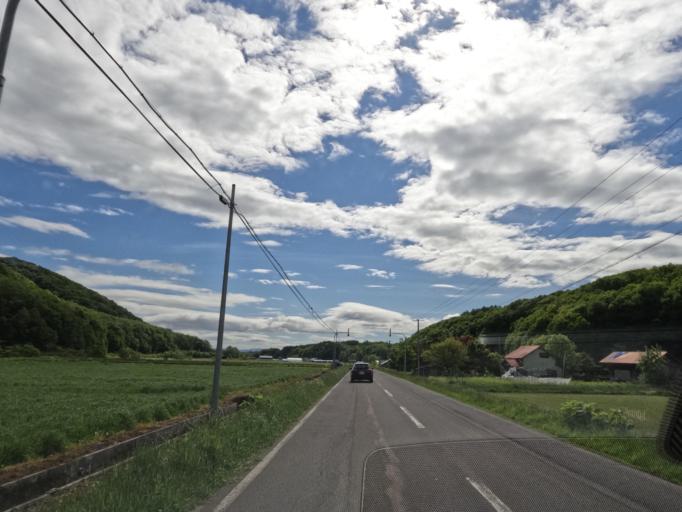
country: JP
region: Hokkaido
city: Kamikawa
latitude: 43.8708
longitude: 142.5728
